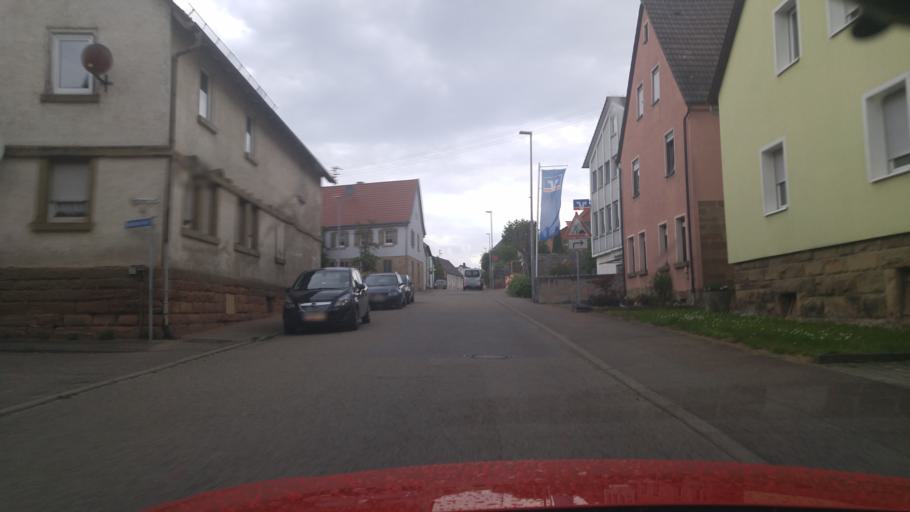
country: DE
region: Baden-Wuerttemberg
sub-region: Regierungsbezirk Stuttgart
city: Gemmingen
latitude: 49.1306
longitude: 9.0065
